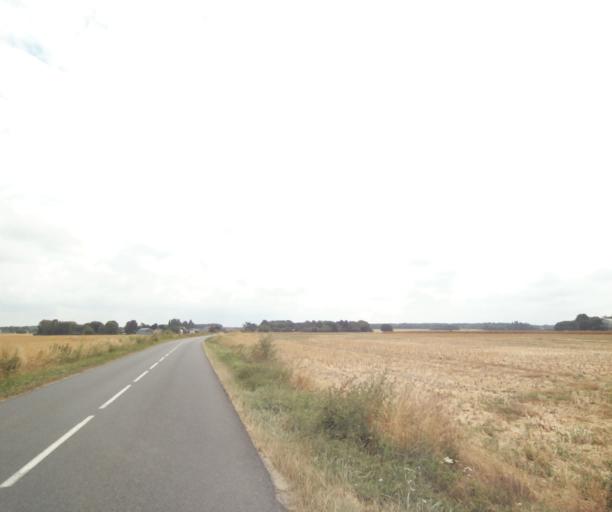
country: FR
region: Centre
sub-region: Departement du Loiret
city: Boigny-sur-Bionne
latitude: 47.9322
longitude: 2.0368
